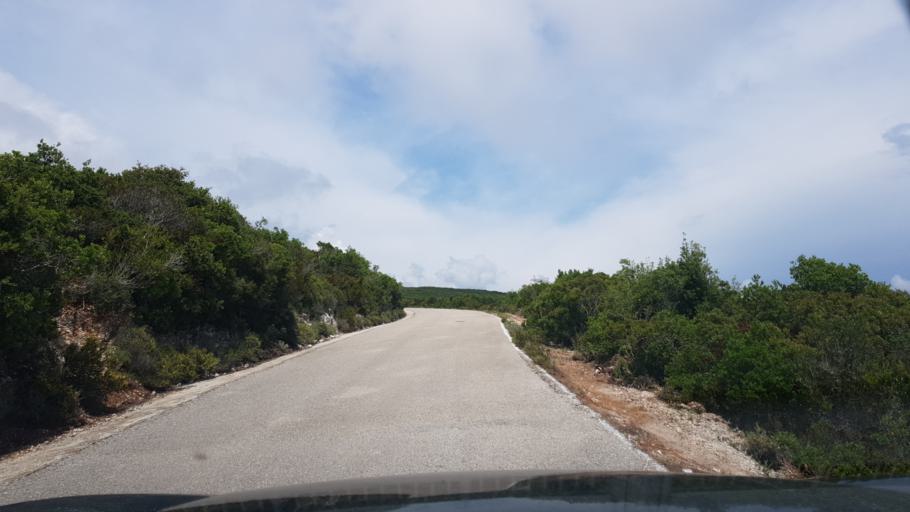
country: GR
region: Ionian Islands
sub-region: Lefkada
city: Nidri
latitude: 38.5969
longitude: 20.5553
